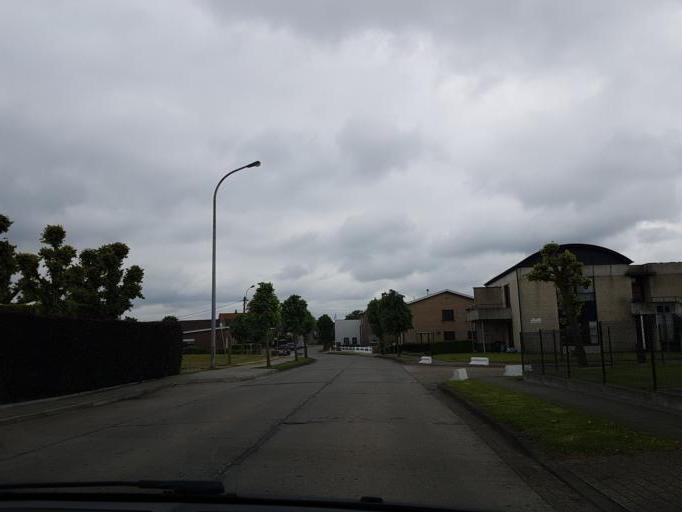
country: BE
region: Flanders
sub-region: Provincie Oost-Vlaanderen
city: Aalter
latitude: 51.1299
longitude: 3.4890
